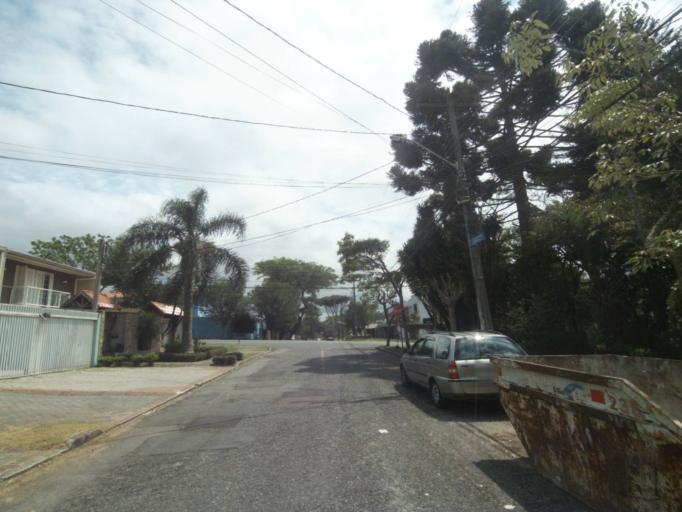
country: BR
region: Parana
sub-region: Pinhais
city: Pinhais
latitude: -25.4334
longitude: -49.2260
